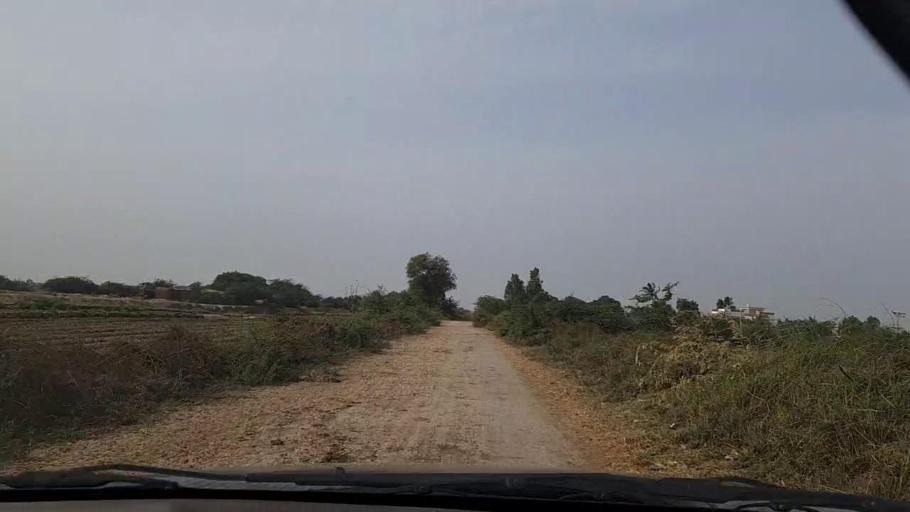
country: PK
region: Sindh
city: Thatta
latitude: 24.5686
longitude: 67.8614
